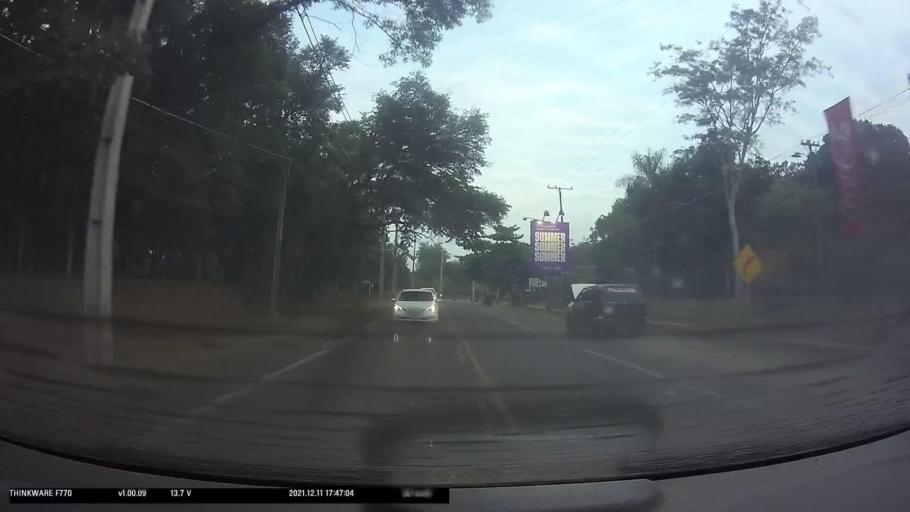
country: PY
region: Cordillera
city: San Bernardino
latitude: -25.2976
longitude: -57.2847
